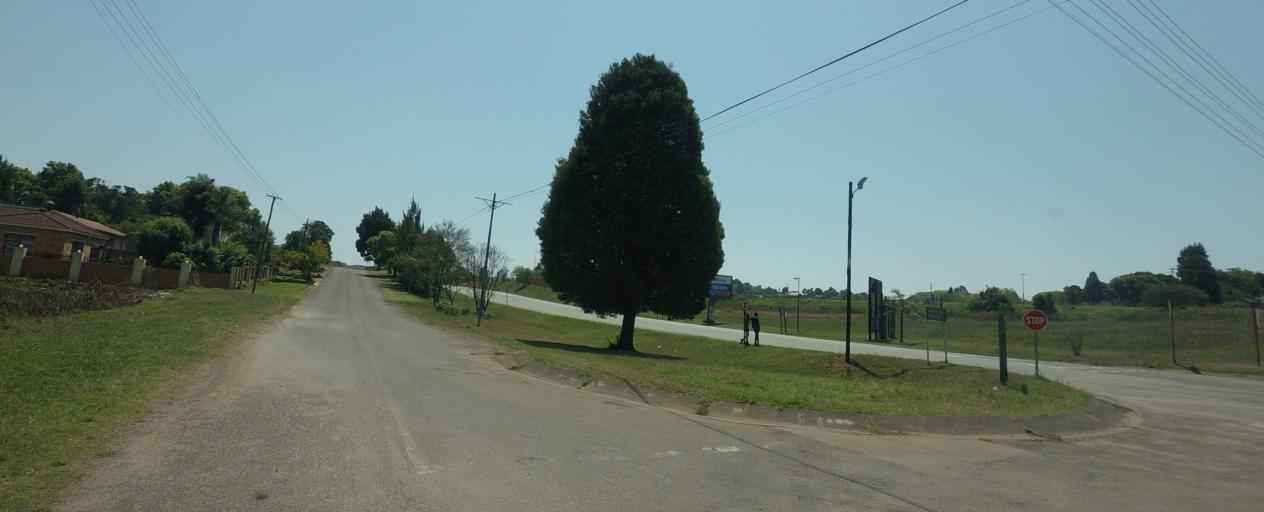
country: ZA
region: Mpumalanga
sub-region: Ehlanzeni District
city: Graksop
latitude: -24.9318
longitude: 30.8374
